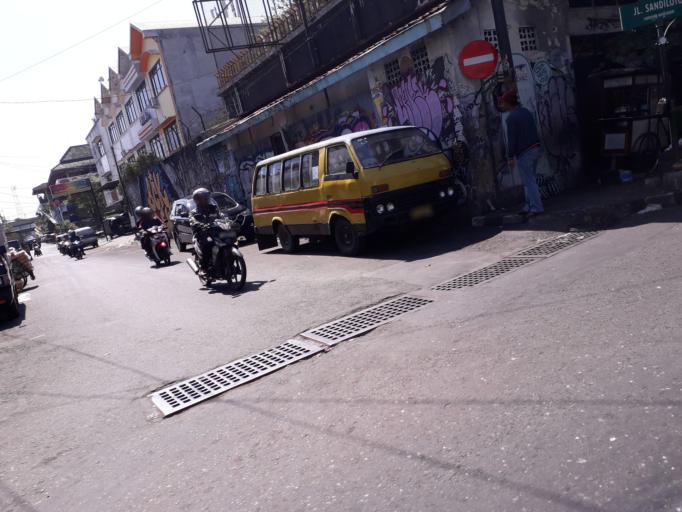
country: ID
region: Daerah Istimewa Yogyakarta
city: Yogyakarta
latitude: -7.7994
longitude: 110.3694
